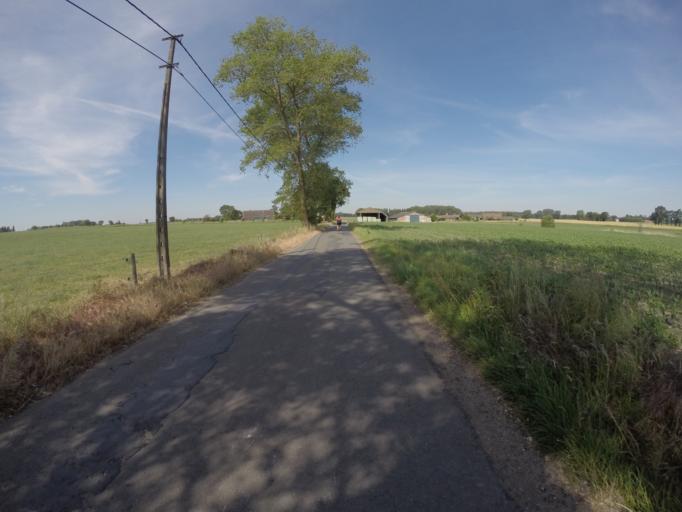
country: BE
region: Flanders
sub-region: Provincie West-Vlaanderen
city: Beernem
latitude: 51.1856
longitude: 3.3582
